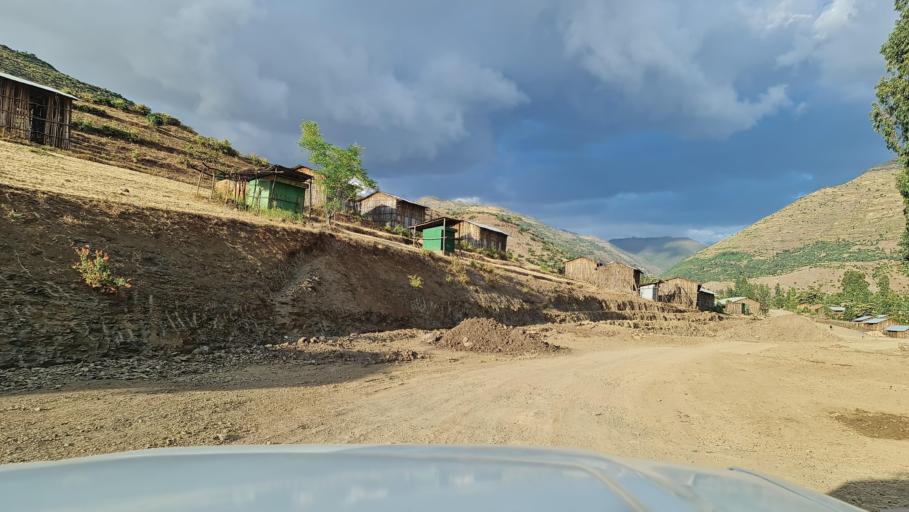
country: ET
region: Amhara
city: Debark'
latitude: 13.0372
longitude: 38.0474
